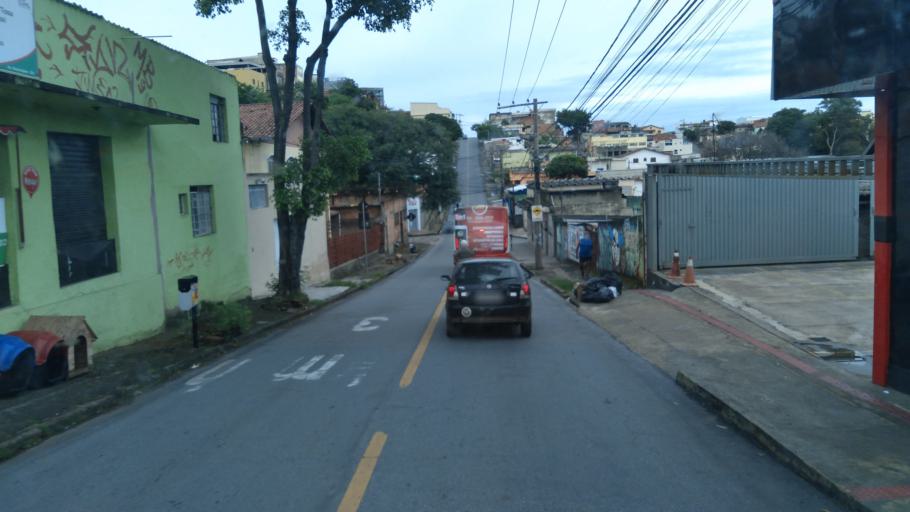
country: BR
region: Minas Gerais
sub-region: Contagem
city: Contagem
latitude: -19.9044
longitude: -44.0105
